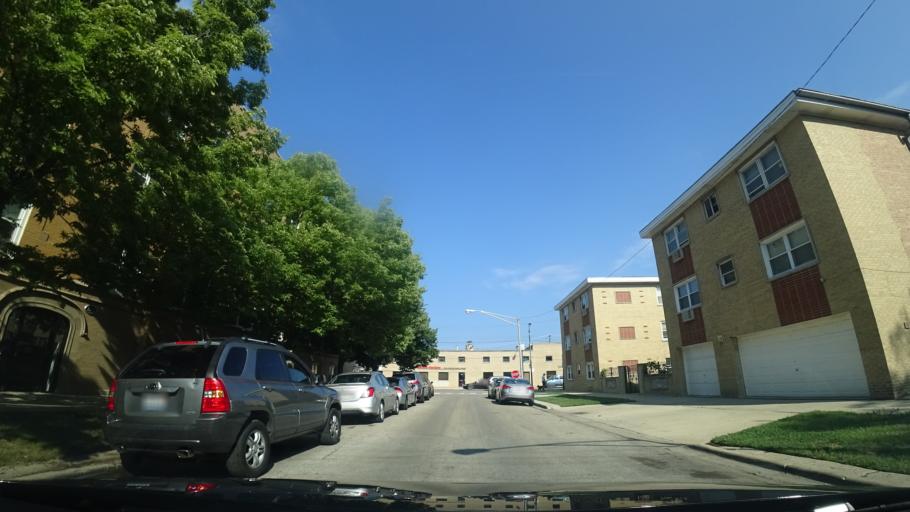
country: US
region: Illinois
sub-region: Cook County
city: Lincolnwood
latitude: 41.9776
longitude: -87.7095
